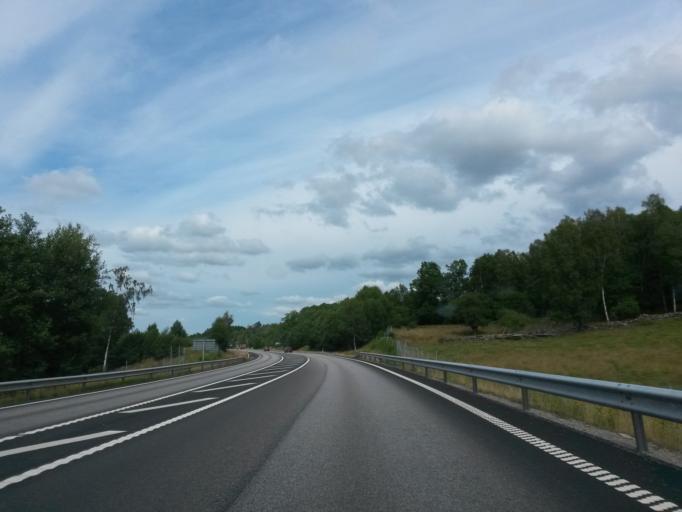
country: SE
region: Vaestra Goetaland
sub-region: Marks Kommun
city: Kinna
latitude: 57.4858
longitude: 12.6803
